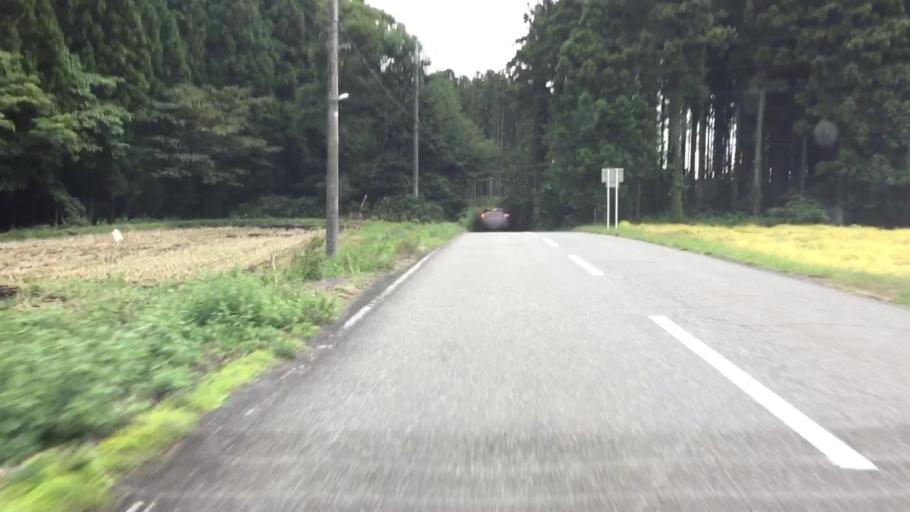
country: JP
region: Tochigi
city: Imaichi
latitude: 36.7689
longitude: 139.7020
